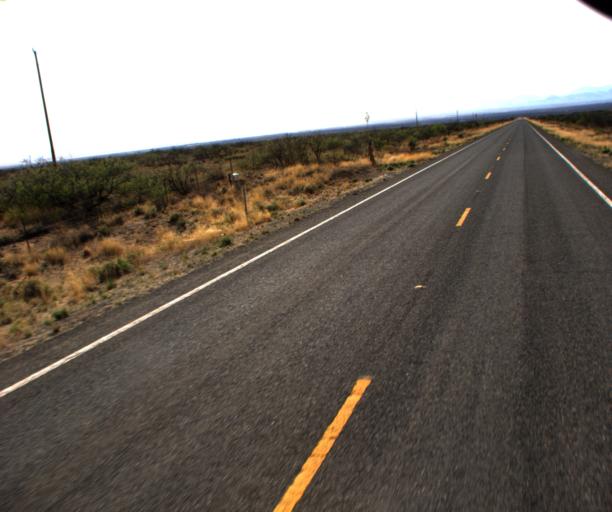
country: US
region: Arizona
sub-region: Cochise County
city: Willcox
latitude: 32.1896
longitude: -109.6888
